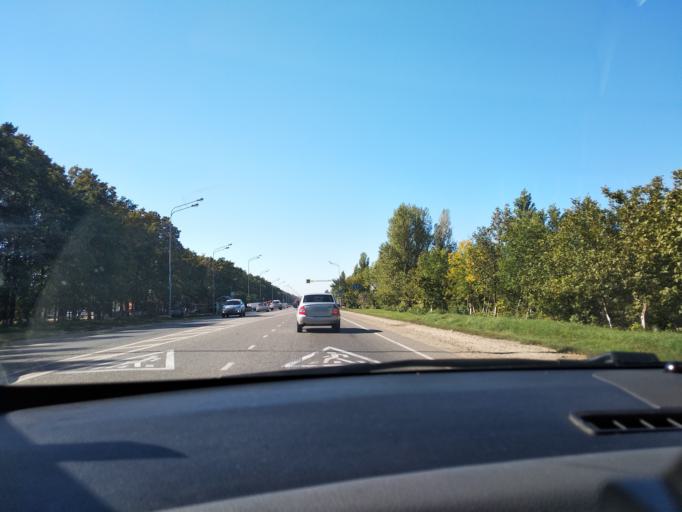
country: RU
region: Krasnodarskiy
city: Novotitarovskaya
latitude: 45.1443
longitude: 39.0462
